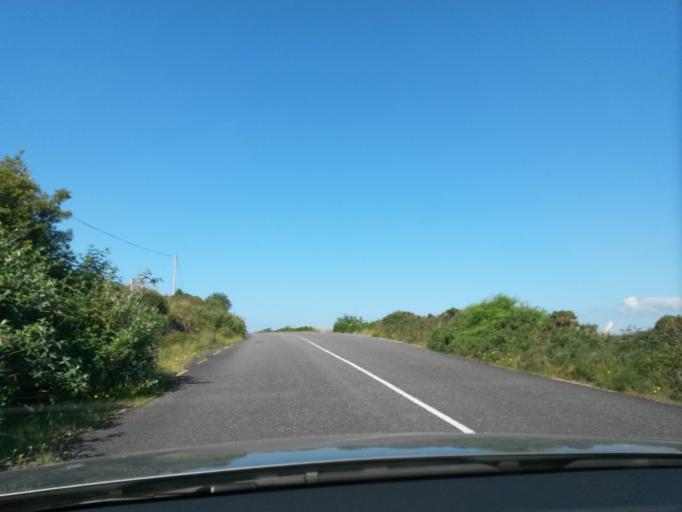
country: IE
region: Munster
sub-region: Ciarrai
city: Kenmare
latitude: 51.7657
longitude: -9.8317
